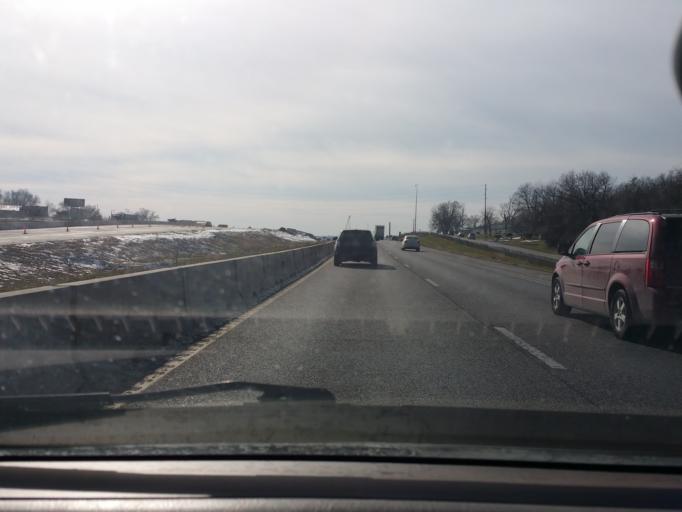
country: US
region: Missouri
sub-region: Clay County
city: Pleasant Valley
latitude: 39.2221
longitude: -94.4715
